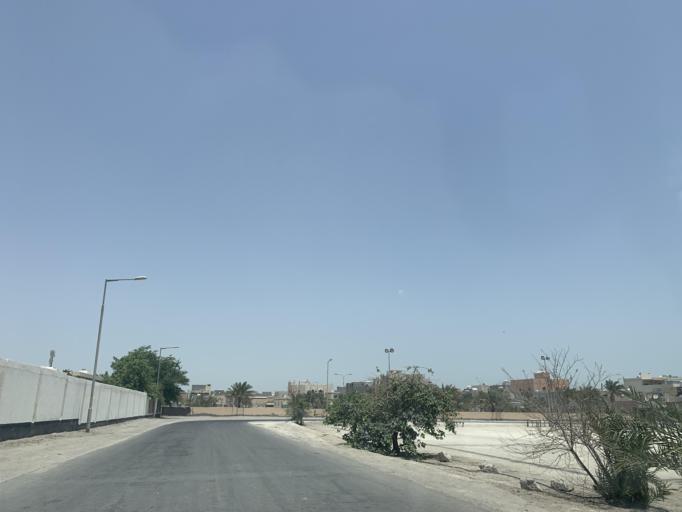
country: BH
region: Northern
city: Sitrah
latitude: 26.1560
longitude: 50.6227
